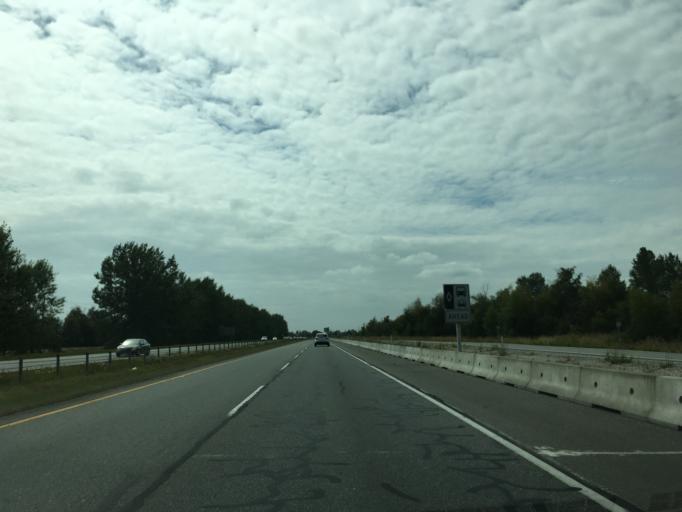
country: CA
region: British Columbia
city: Ladner
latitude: 49.0905
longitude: -122.9912
